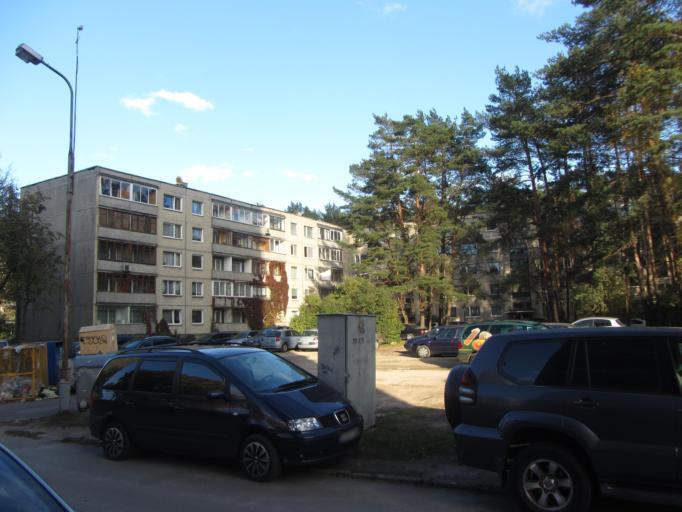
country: LT
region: Vilnius County
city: Lazdynai
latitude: 54.6765
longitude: 25.2170
